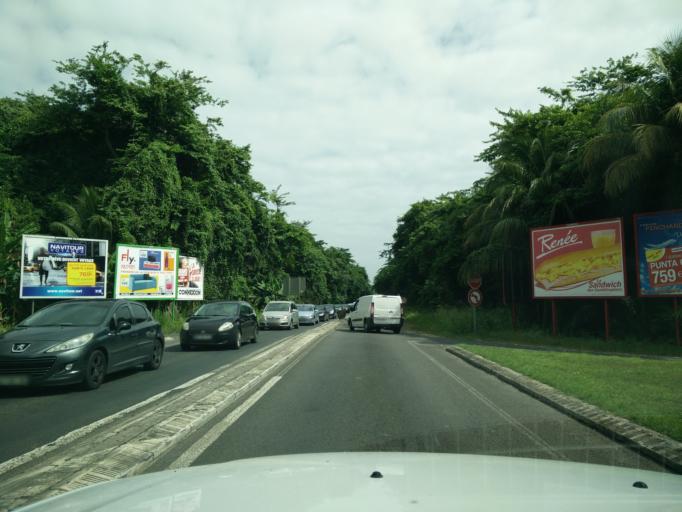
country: GP
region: Guadeloupe
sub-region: Guadeloupe
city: Baie-Mahault
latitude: 16.2514
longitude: -61.5707
